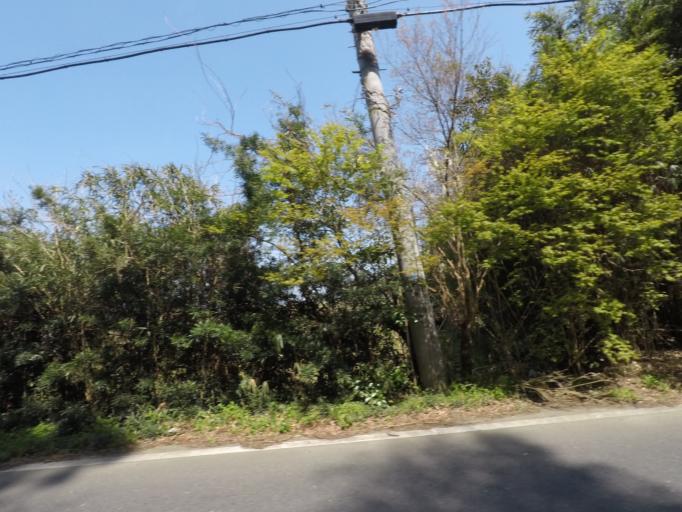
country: JP
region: Chiba
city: Yokaichiba
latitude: 35.6879
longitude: 140.4618
